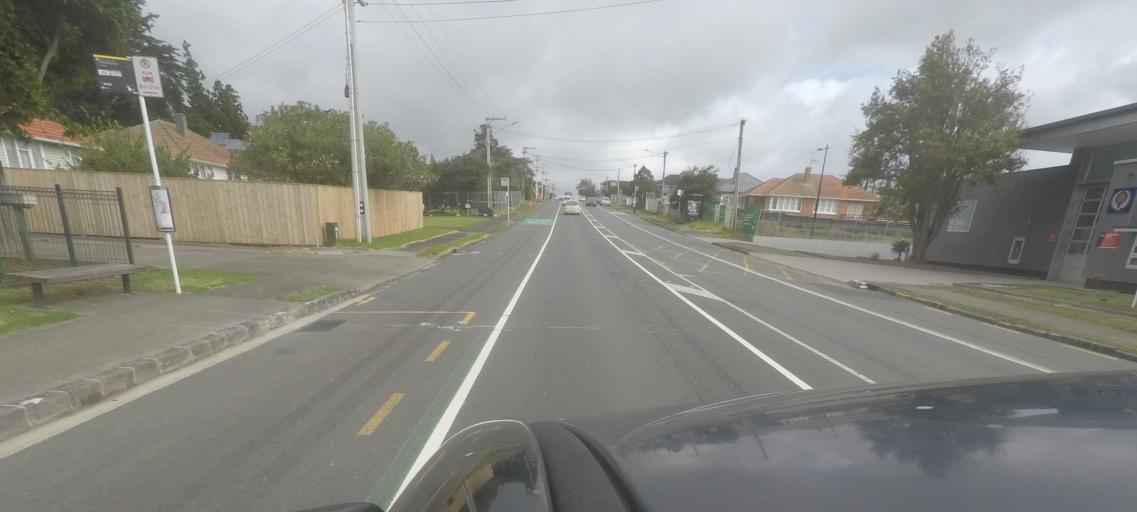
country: NZ
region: Auckland
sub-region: Auckland
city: Auckland
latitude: -36.9157
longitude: 174.7381
